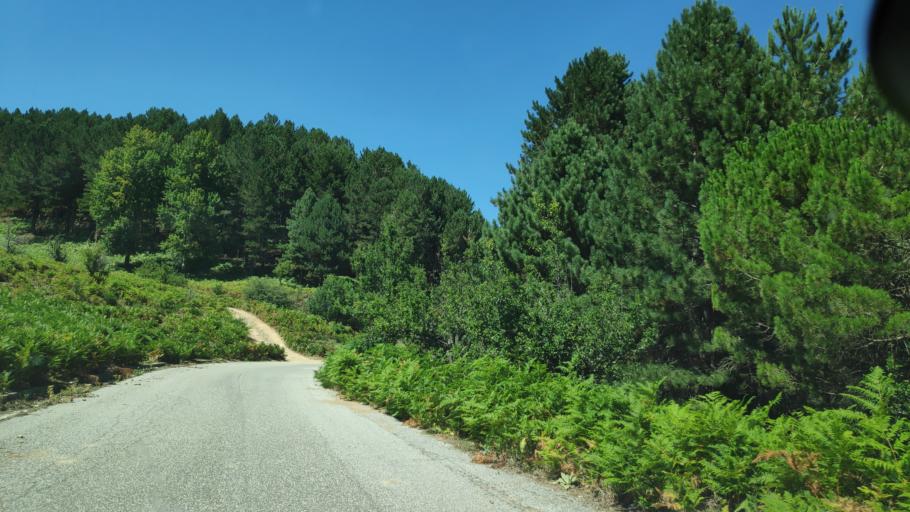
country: IT
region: Calabria
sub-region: Provincia di Reggio Calabria
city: Bova
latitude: 38.0319
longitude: 15.9460
